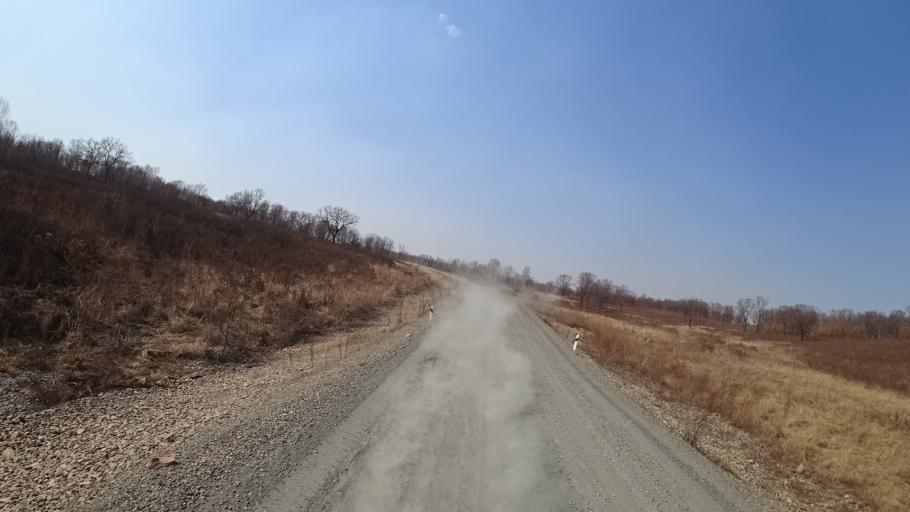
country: RU
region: Amur
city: Novobureyskiy
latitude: 49.8246
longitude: 129.9958
